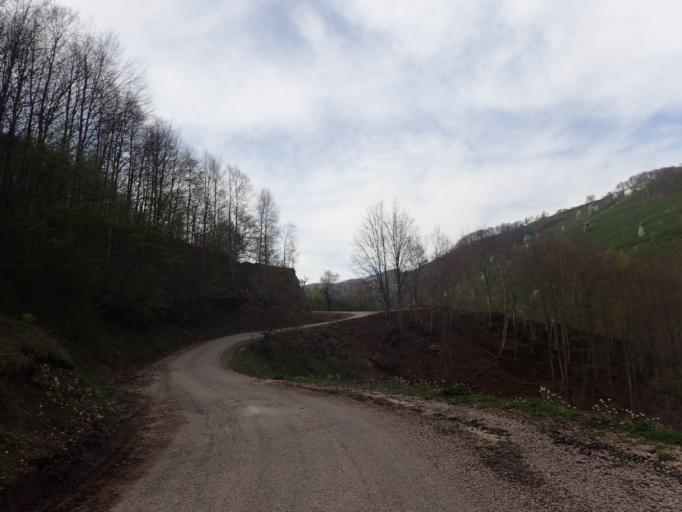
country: TR
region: Ordu
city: Aybasti
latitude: 40.7120
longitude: 37.2806
